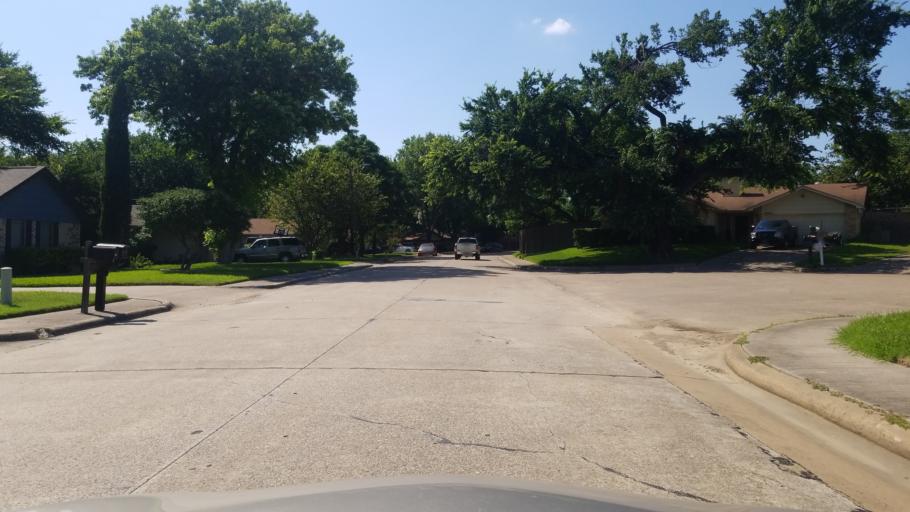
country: US
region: Texas
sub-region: Dallas County
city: Grand Prairie
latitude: 32.6774
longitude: -97.0142
